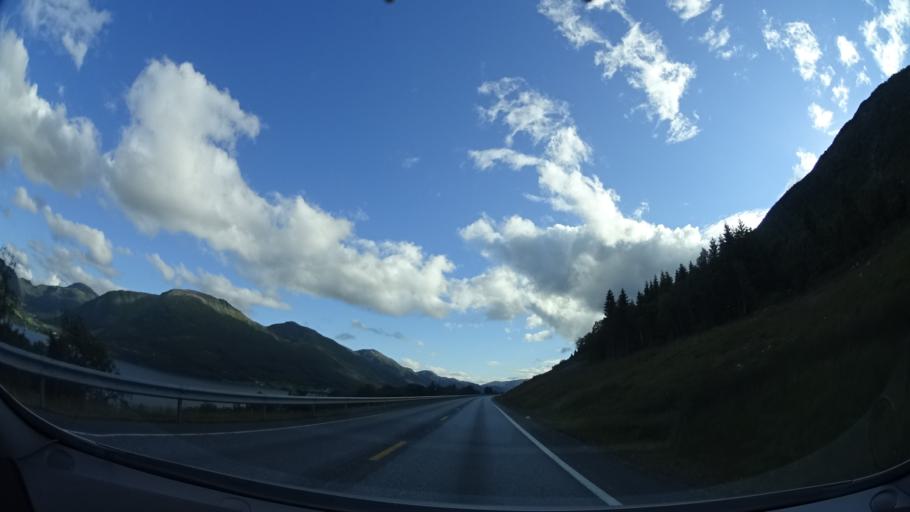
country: NO
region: More og Romsdal
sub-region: Gjemnes
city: Batnfjordsora
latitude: 62.9371
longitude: 7.7336
